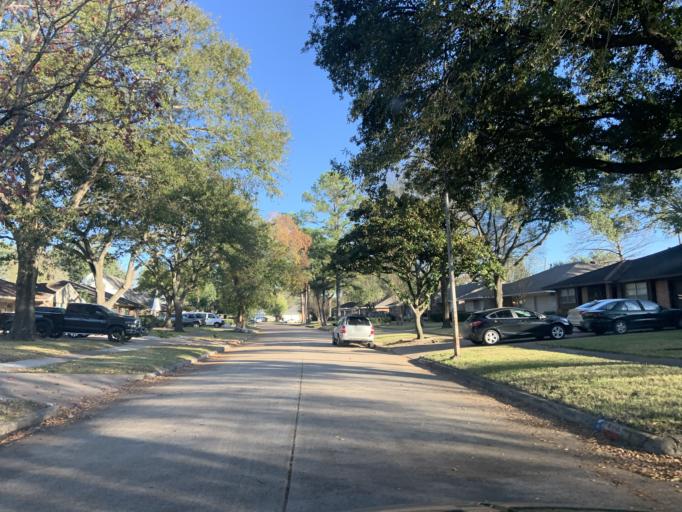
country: US
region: Texas
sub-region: Harris County
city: Bellaire
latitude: 29.6897
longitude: -95.5204
